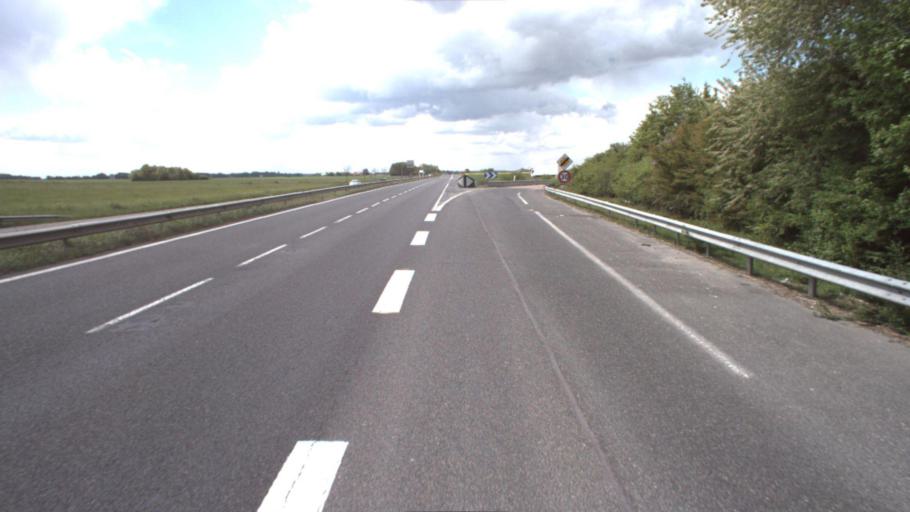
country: FR
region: Ile-de-France
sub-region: Departement de Seine-et-Marne
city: Touquin
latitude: 48.6857
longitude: 3.0227
